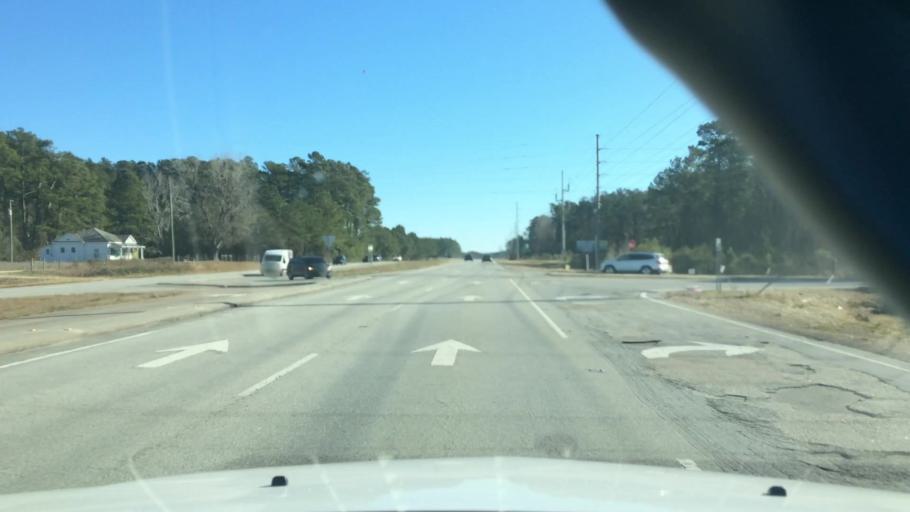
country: US
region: North Carolina
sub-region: Brunswick County
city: Shallotte
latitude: 33.9545
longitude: -78.4488
